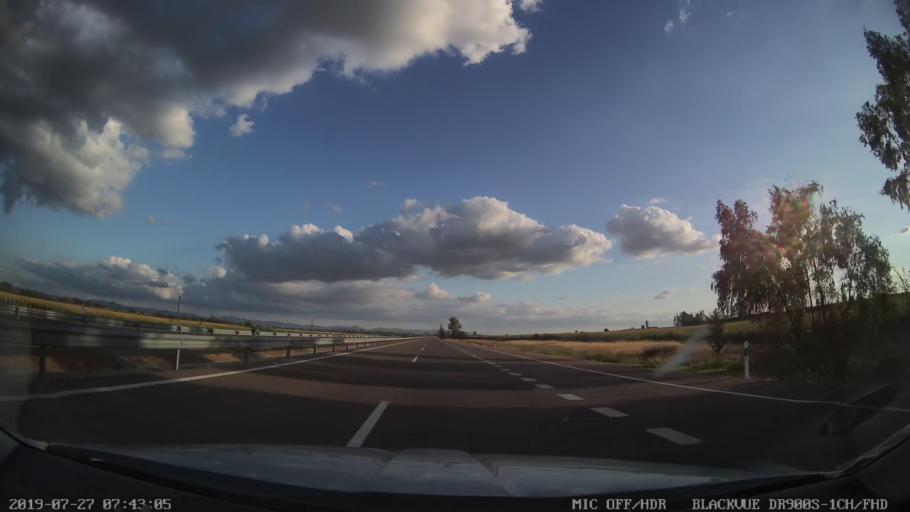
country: ES
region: Extremadura
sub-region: Provincia de Badajoz
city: Santa Amalia
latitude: 39.0013
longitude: -6.0937
